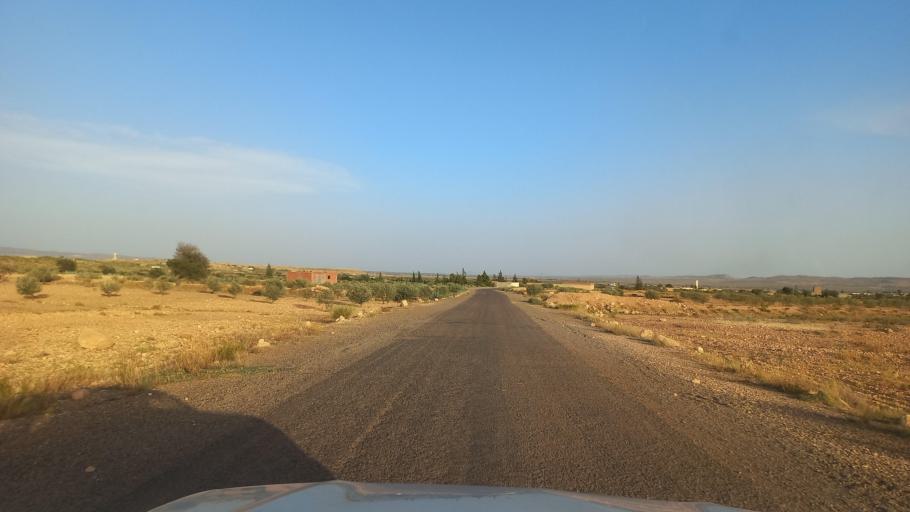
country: TN
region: Al Qasrayn
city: Kasserine
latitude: 35.2723
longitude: 8.9261
